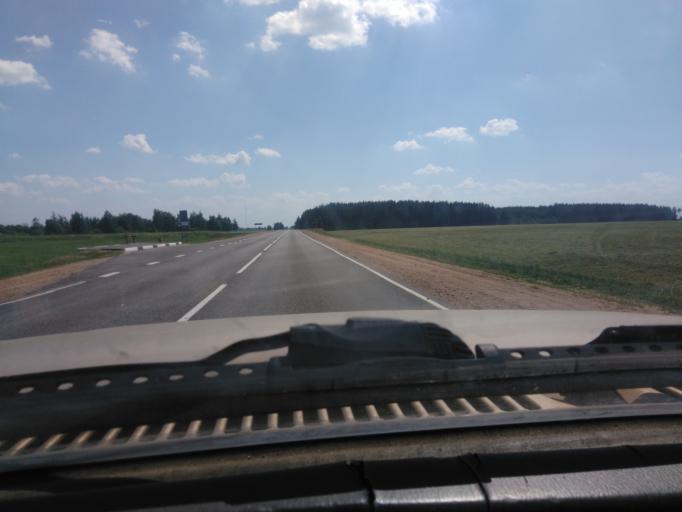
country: BY
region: Mogilev
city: Kamyennyya Lavy
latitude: 54.0542
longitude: 30.3263
